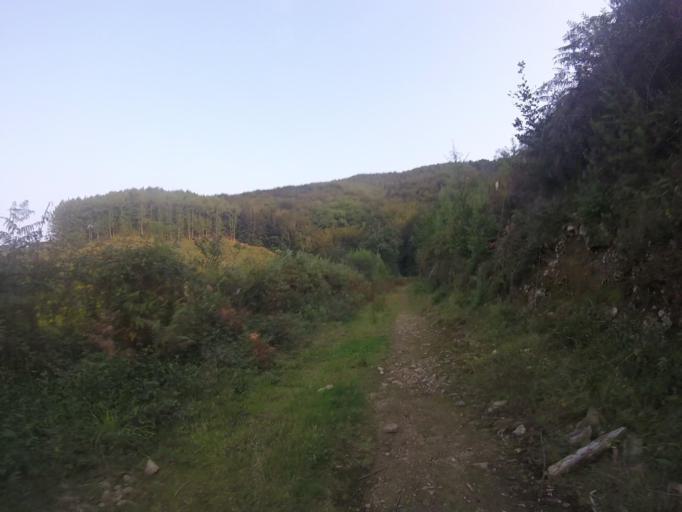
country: ES
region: Navarre
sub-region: Provincia de Navarra
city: Arano
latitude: 43.2592
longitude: -1.8371
